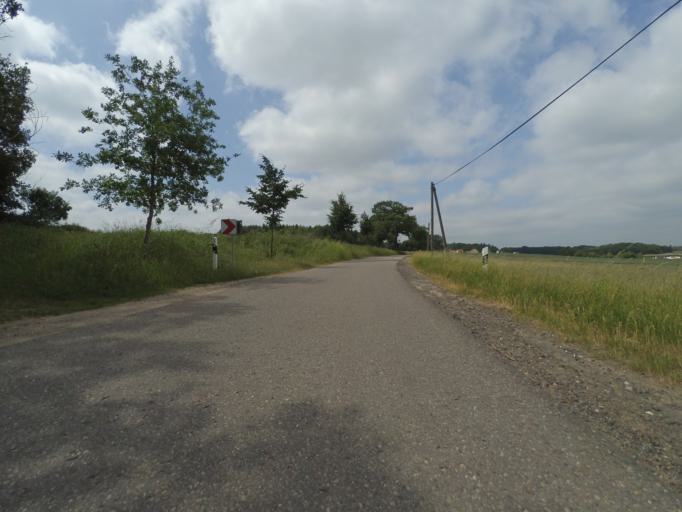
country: DE
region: Mecklenburg-Vorpommern
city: Klink
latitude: 53.4768
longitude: 12.5275
